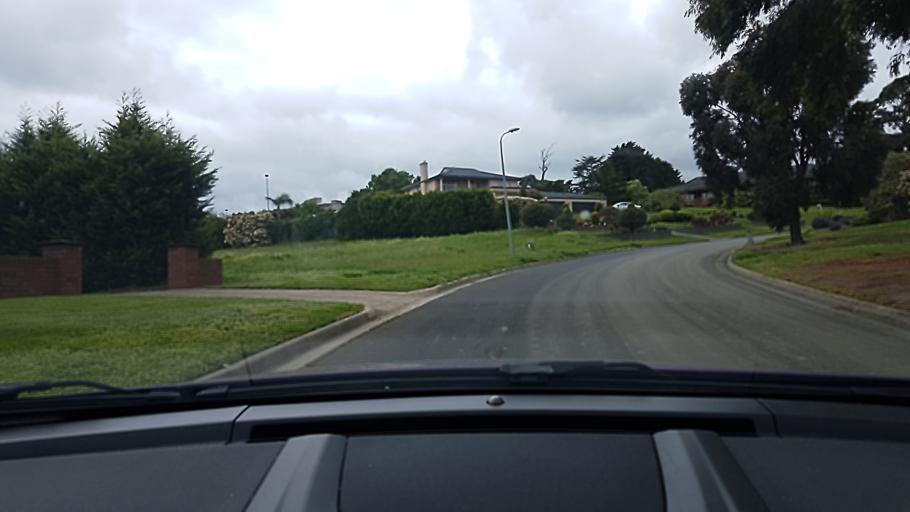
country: AU
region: Victoria
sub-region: Nillumbik
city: Eltham
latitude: -37.7495
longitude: 145.1394
